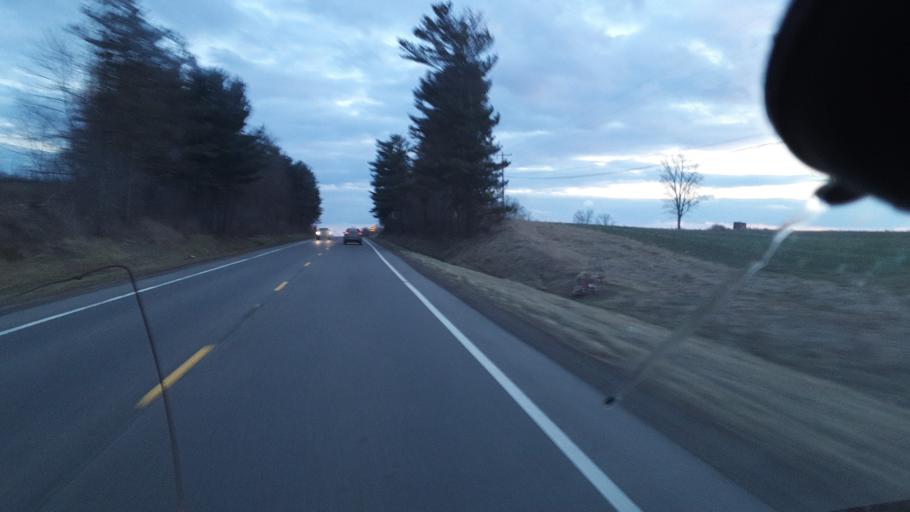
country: US
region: Ohio
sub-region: Perry County
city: Thornport
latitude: 39.8599
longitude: -82.3948
